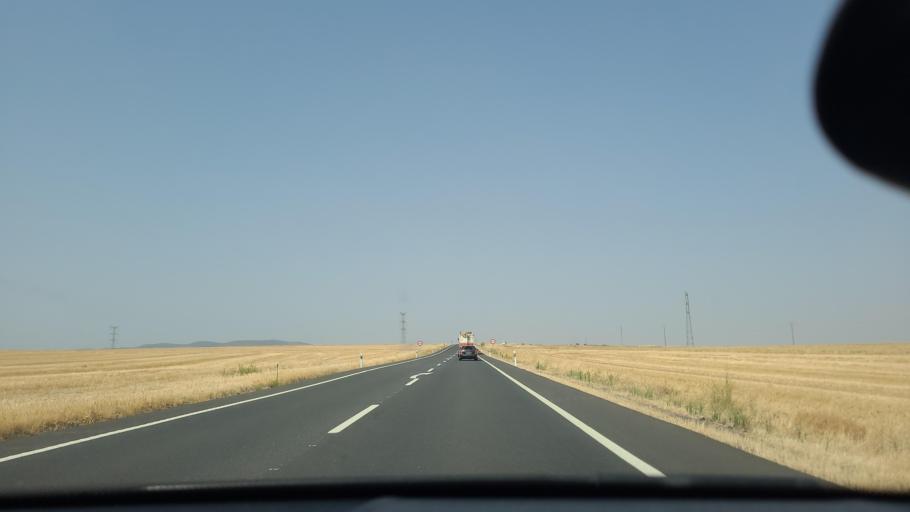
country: ES
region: Extremadura
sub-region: Provincia de Badajoz
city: Ahillones
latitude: 38.2564
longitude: -5.8966
